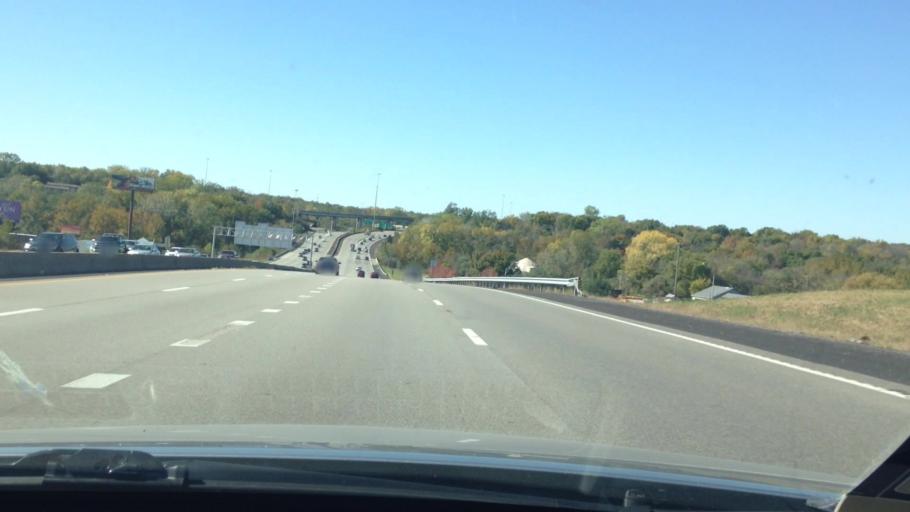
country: US
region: Missouri
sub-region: Platte County
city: Riverside
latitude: 39.1888
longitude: -94.6047
